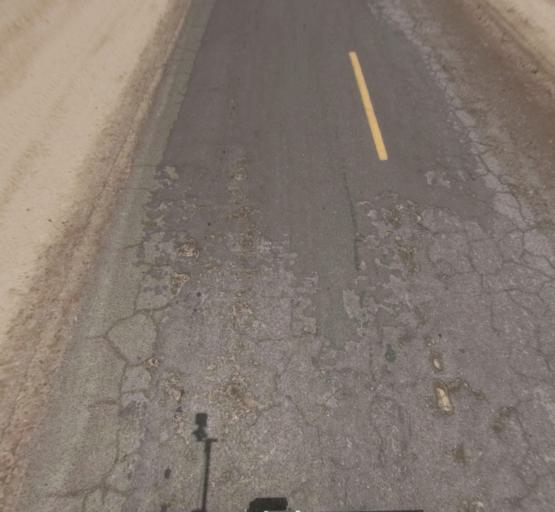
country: US
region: California
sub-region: Fresno County
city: Kerman
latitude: 36.8221
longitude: -120.1982
